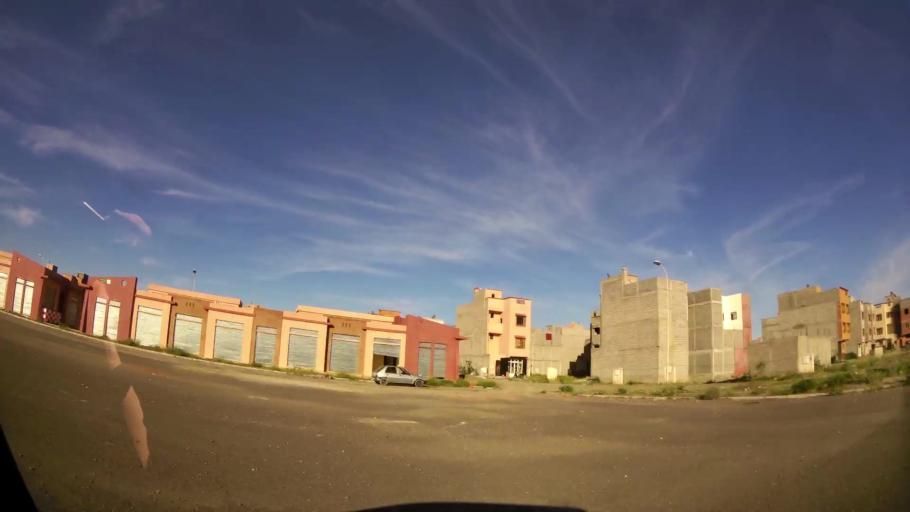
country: MA
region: Marrakech-Tensift-Al Haouz
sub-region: Marrakech
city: Marrakesh
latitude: 31.7621
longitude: -8.1043
